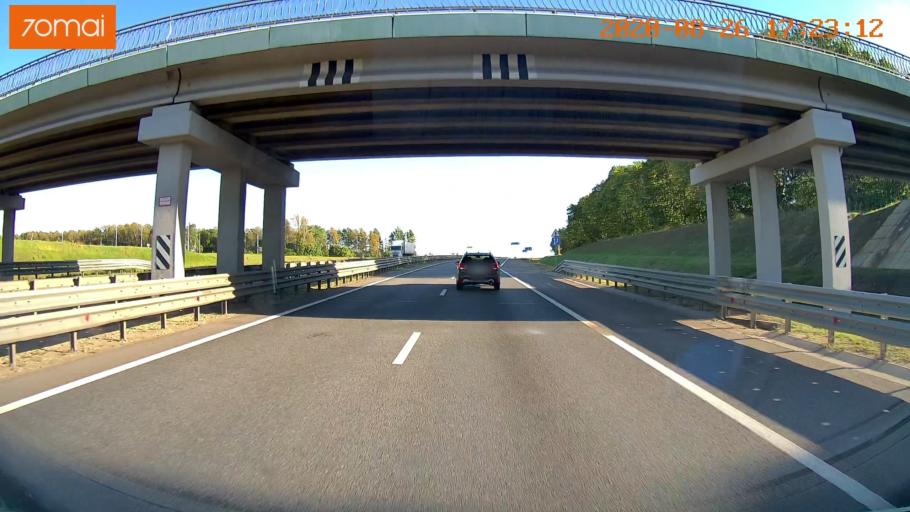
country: RU
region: Tula
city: Volovo
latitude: 53.5384
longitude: 38.1181
